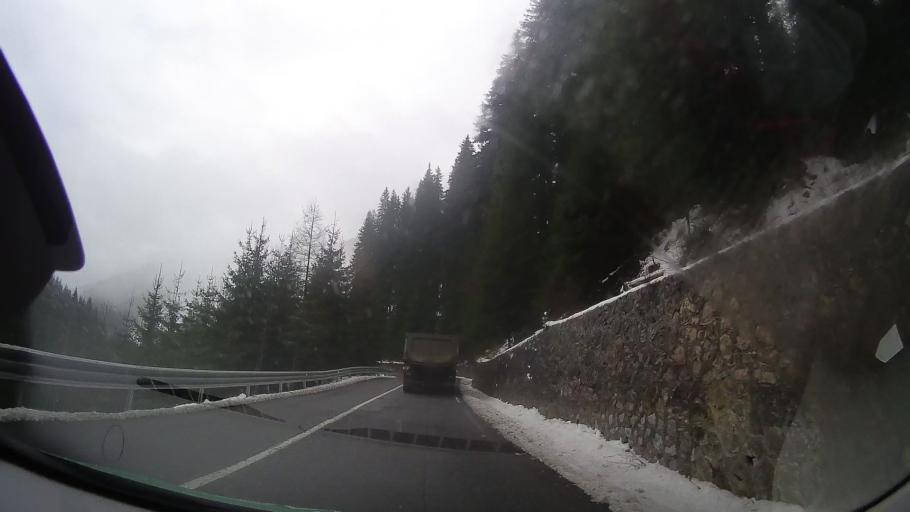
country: RO
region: Neamt
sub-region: Comuna Bicaz Chei
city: Bicaz Chei
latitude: 46.7819
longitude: 25.7485
